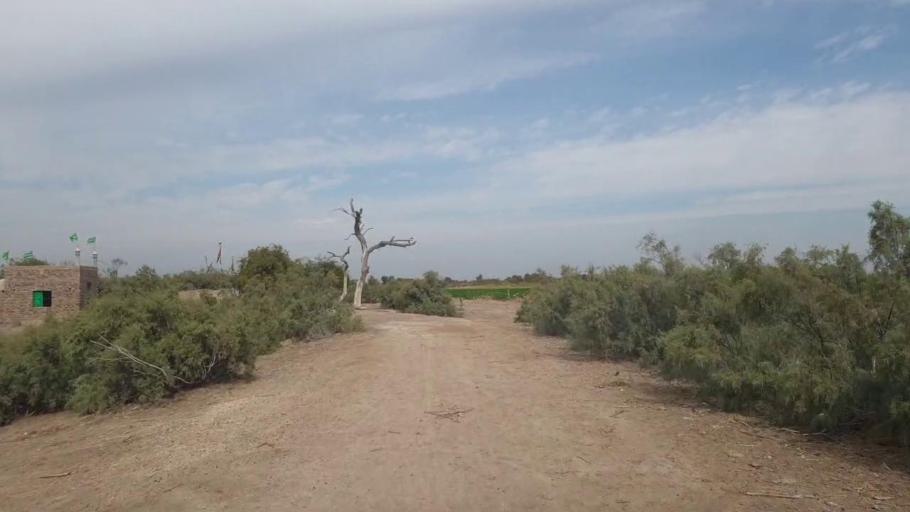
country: PK
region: Sindh
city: Sanghar
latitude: 26.0554
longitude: 68.9087
